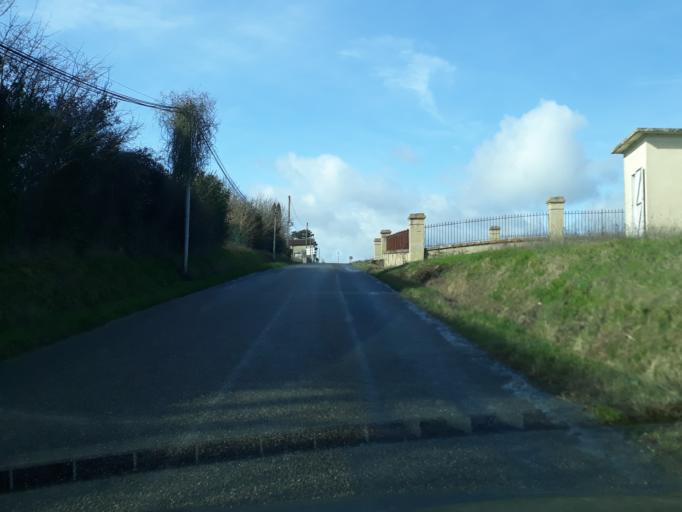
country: FR
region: Midi-Pyrenees
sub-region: Departement du Gers
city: Pujaudran
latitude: 43.6163
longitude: 1.0612
